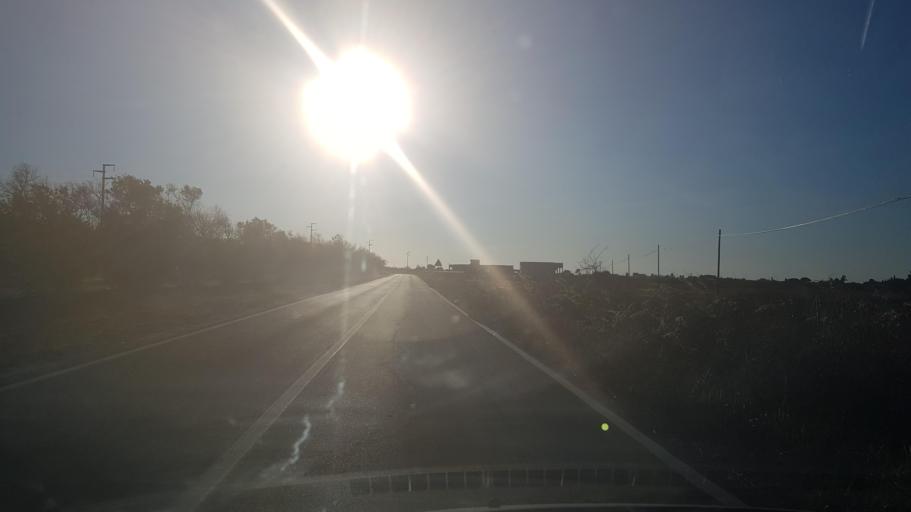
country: IT
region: Apulia
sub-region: Provincia di Lecce
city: Struda
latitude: 40.3284
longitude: 18.3082
